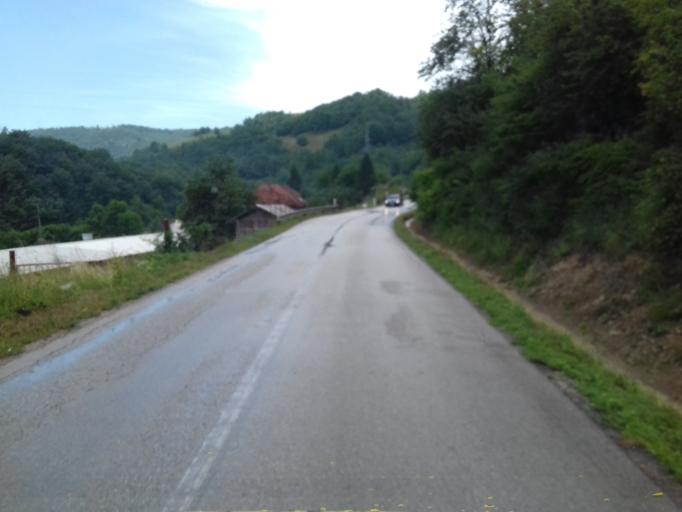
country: BA
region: Federation of Bosnia and Herzegovina
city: Kiseljak
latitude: 43.9536
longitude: 18.1272
